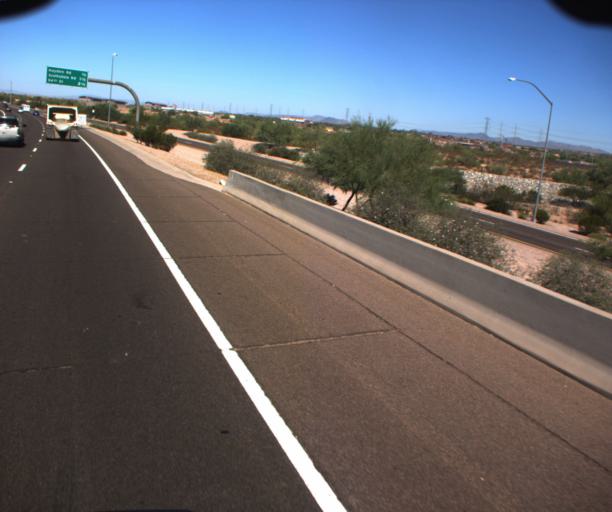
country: US
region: Arizona
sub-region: Maricopa County
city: Paradise Valley
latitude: 33.6479
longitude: -111.8937
